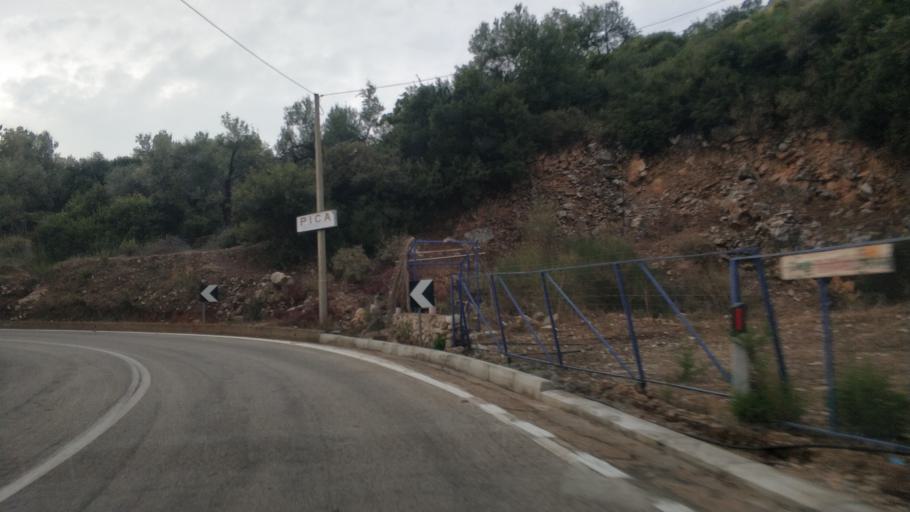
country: AL
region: Vlore
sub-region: Rrethi i Sarandes
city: Lukove
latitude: 40.0153
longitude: 19.8960
